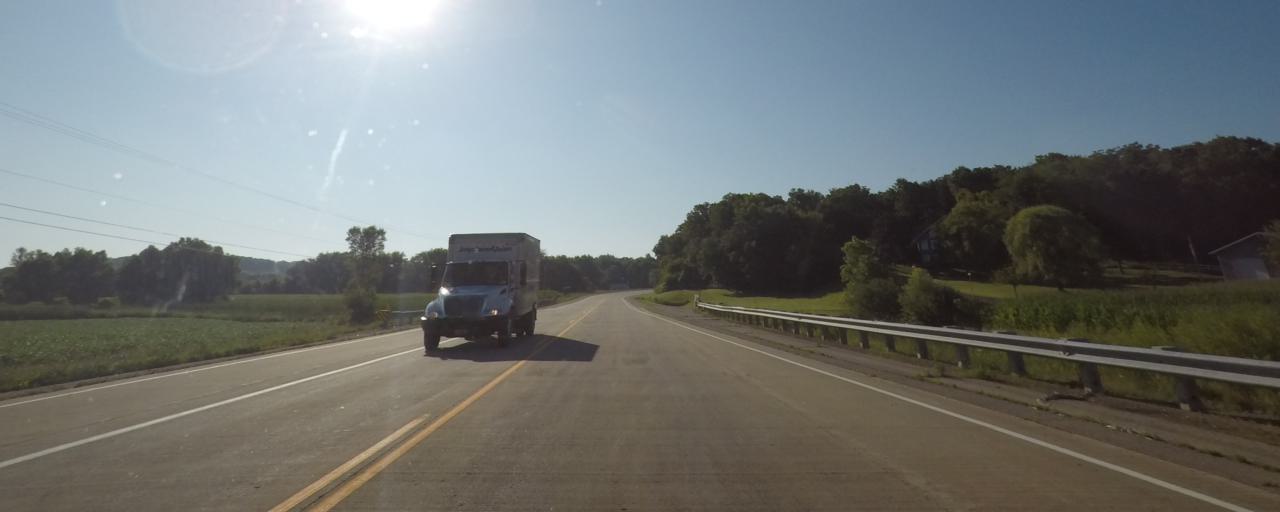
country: US
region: Wisconsin
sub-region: Jefferson County
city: Lake Koshkonong
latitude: 42.9724
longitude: -88.9222
